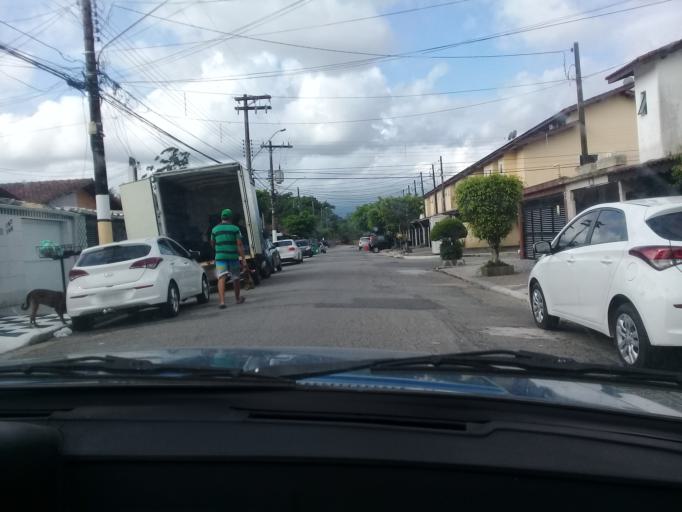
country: BR
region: Sao Paulo
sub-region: Guaruja
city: Guaruja
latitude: -23.9891
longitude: -46.2815
